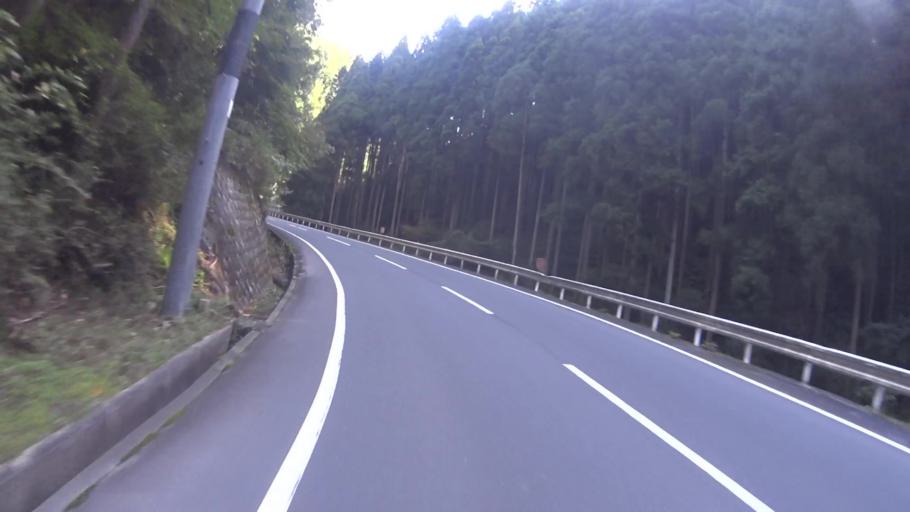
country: JP
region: Kyoto
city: Kameoka
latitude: 35.1270
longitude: 135.5592
